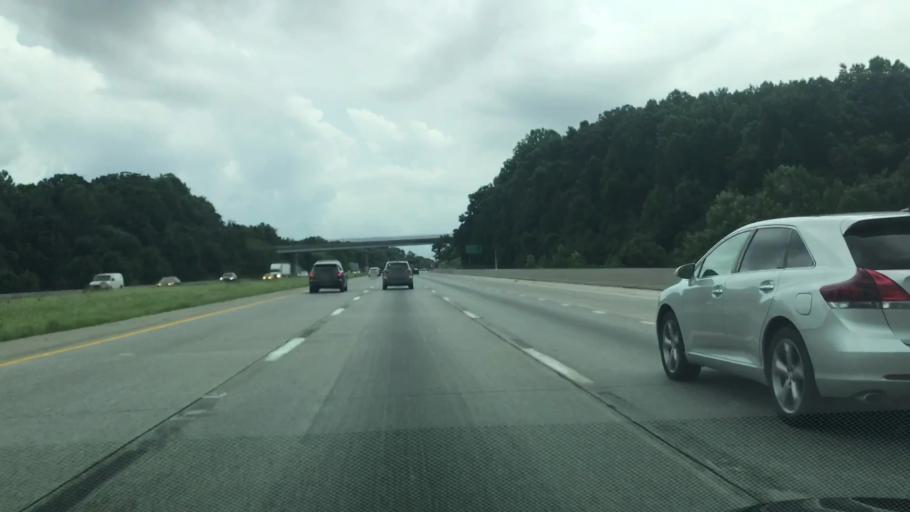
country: US
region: Pennsylvania
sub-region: Northampton County
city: Old Orchard
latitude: 40.6278
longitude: -75.2808
